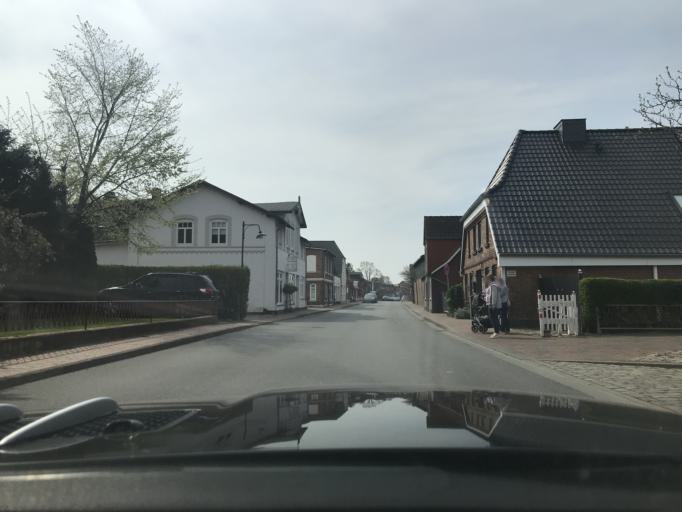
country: DE
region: Schleswig-Holstein
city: Grube
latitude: 54.2340
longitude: 11.0359
